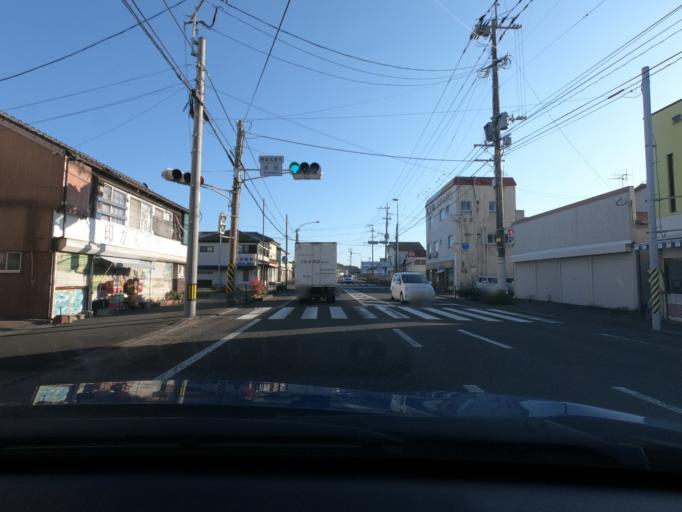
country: JP
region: Kagoshima
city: Akune
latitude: 32.0178
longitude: 130.1973
